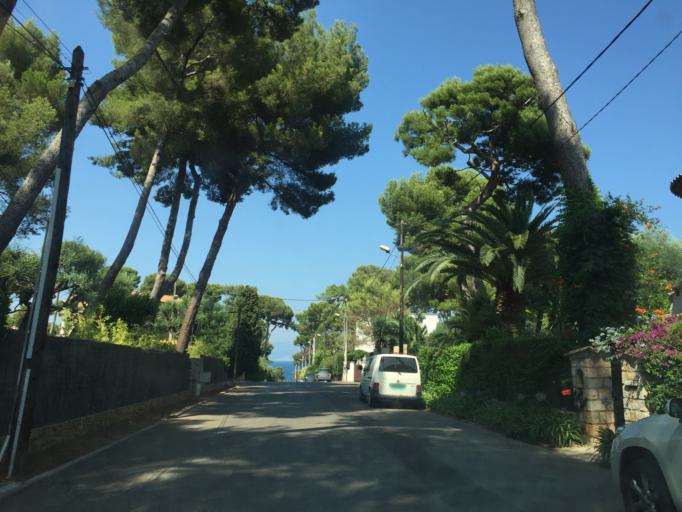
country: FR
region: Provence-Alpes-Cote d'Azur
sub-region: Departement des Alpes-Maritimes
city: Antibes
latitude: 43.5626
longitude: 7.1347
